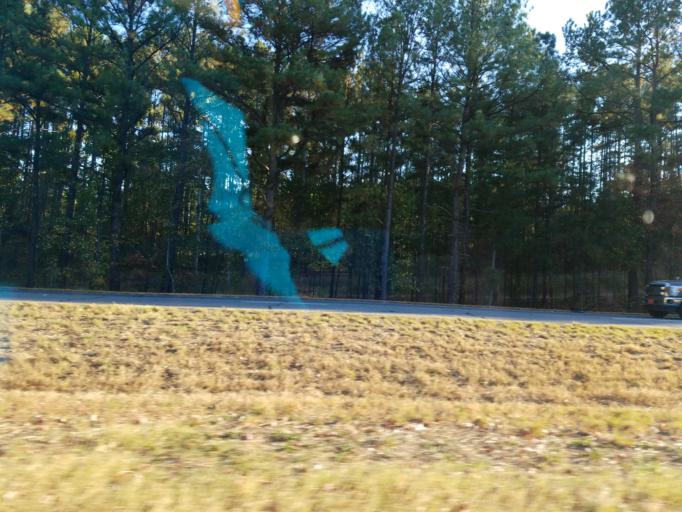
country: US
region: Georgia
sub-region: Bartow County
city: Euharlee
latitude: 34.2190
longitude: -84.9222
